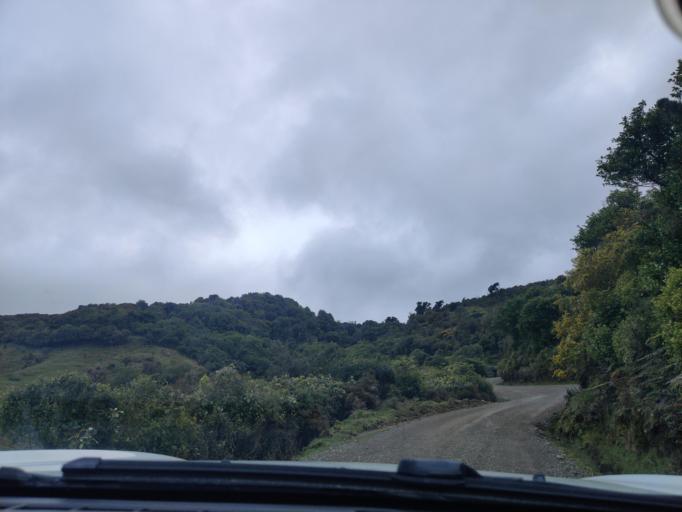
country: NZ
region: Manawatu-Wanganui
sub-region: Palmerston North City
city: Palmerston North
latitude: -40.2736
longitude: 175.8495
